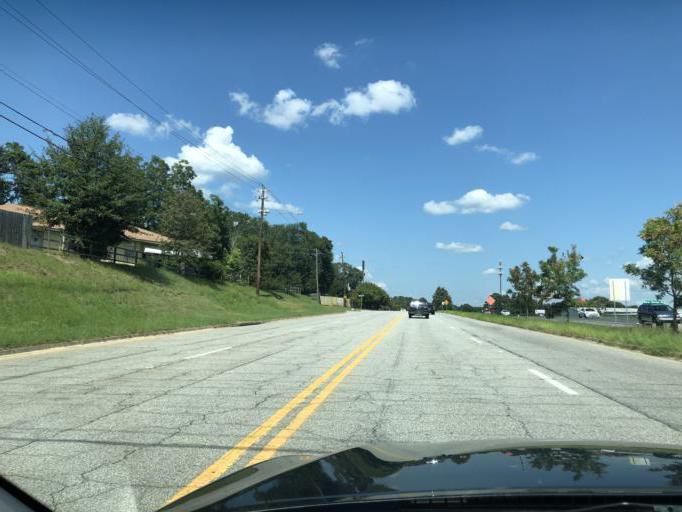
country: US
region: Georgia
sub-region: Muscogee County
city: Columbus
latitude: 32.5114
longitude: -84.9300
